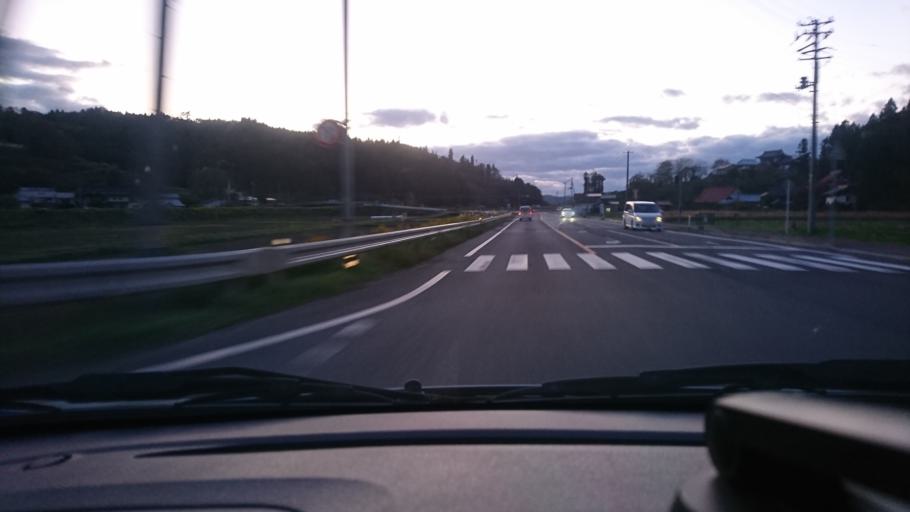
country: JP
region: Iwate
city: Ichinoseki
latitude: 38.8972
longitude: 141.3040
